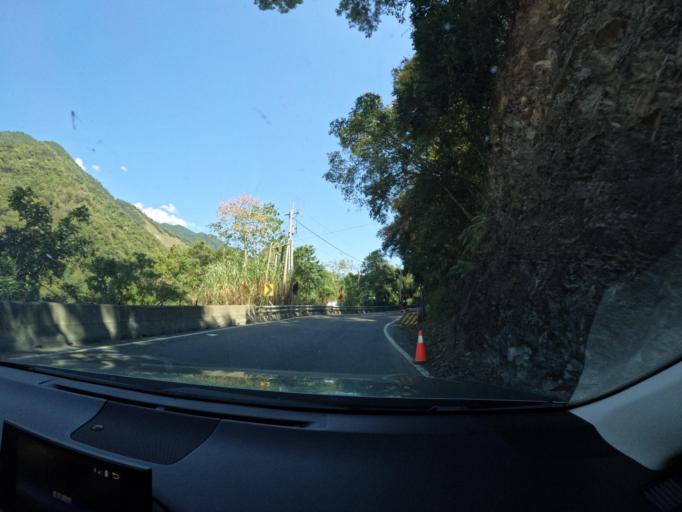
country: TW
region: Taiwan
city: Yujing
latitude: 23.2320
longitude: 120.8107
